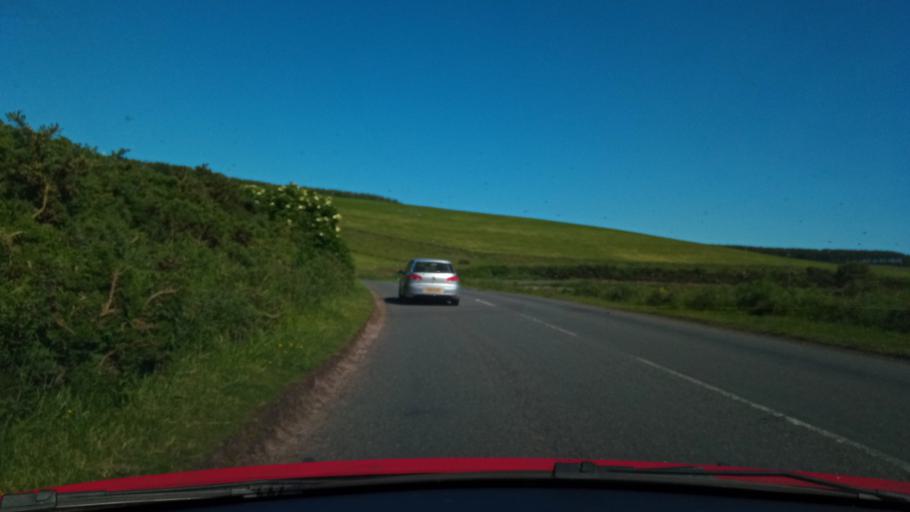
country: GB
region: Scotland
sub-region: The Scottish Borders
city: Duns
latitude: 55.8352
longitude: -2.3343
